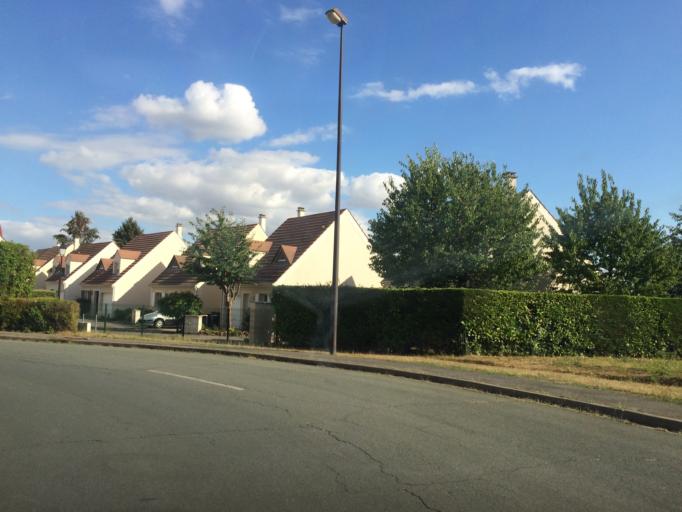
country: FR
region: Ile-de-France
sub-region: Departement de l'Essonne
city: Marolles-en-Hurepoix
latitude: 48.5594
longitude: 2.3104
